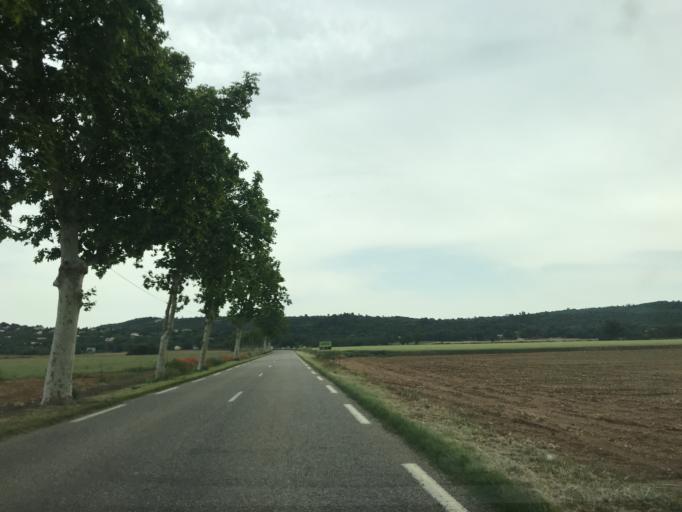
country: FR
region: Provence-Alpes-Cote d'Azur
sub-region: Departement du Var
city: Ginasservis
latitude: 43.6547
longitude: 5.8443
